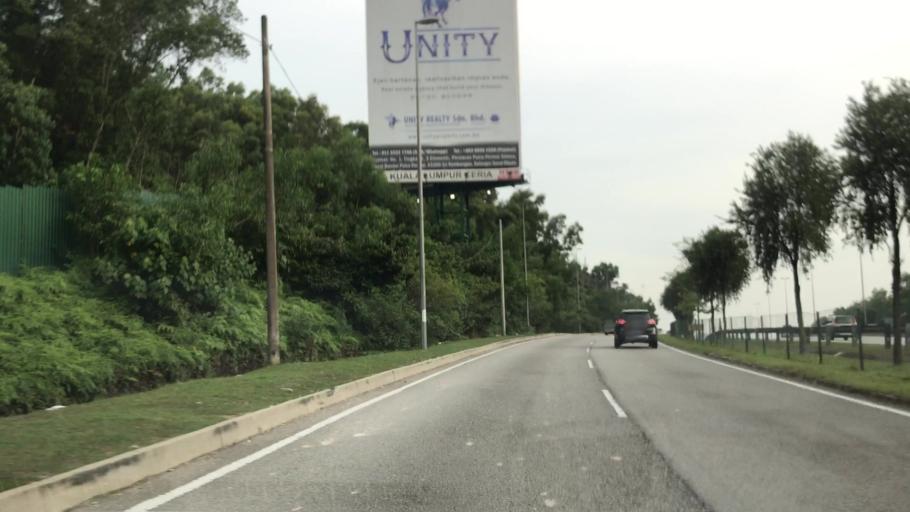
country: MY
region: Kuala Lumpur
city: Kuala Lumpur
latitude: 3.0812
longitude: 101.6923
